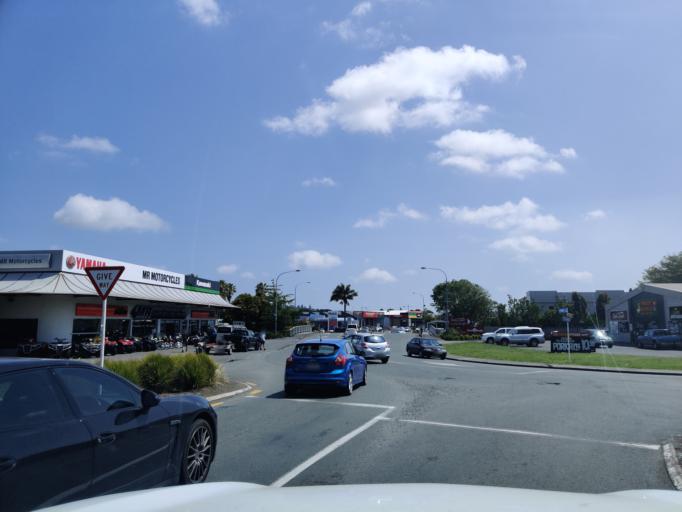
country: NZ
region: Auckland
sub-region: Auckland
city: Pukekohe East
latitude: -37.2007
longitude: 174.9089
